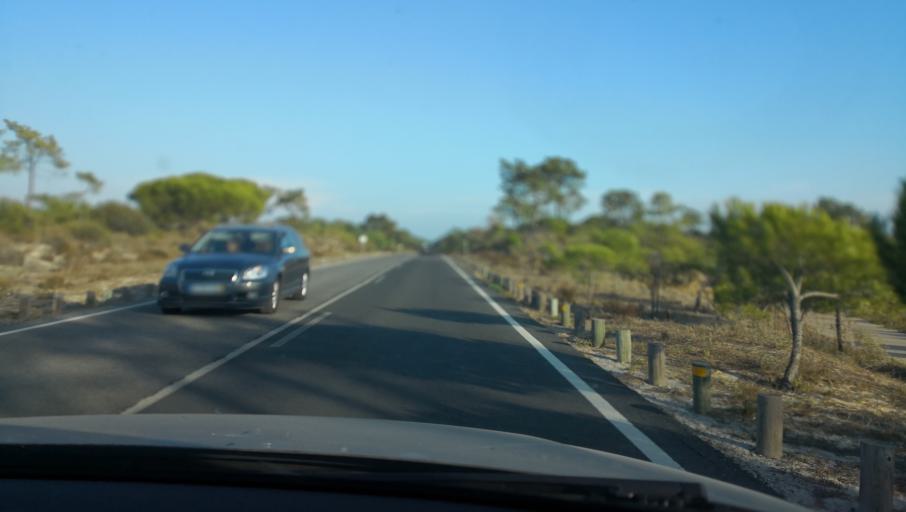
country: PT
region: Setubal
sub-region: Setubal
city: Setubal
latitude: 38.4688
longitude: -8.8818
